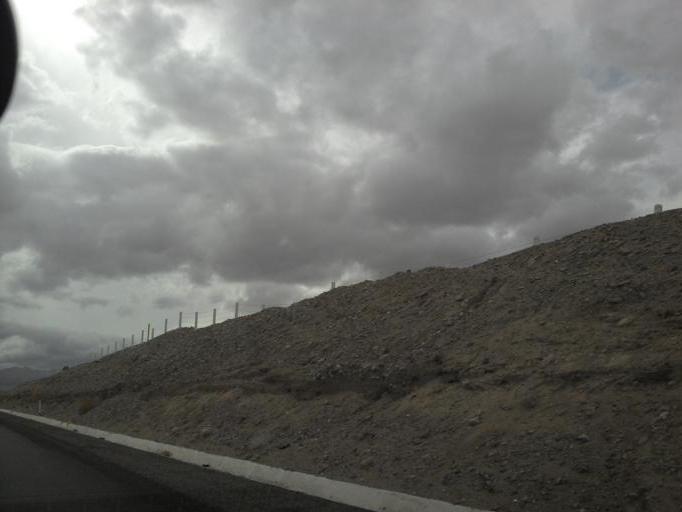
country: MX
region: Baja California
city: Progreso
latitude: 32.5672
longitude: -115.8539
